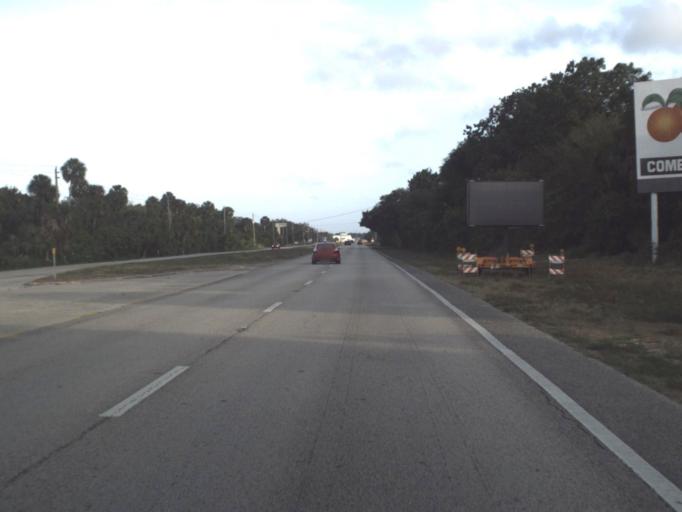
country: US
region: Florida
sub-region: Brevard County
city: Rockledge
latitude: 28.3095
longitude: -80.7081
